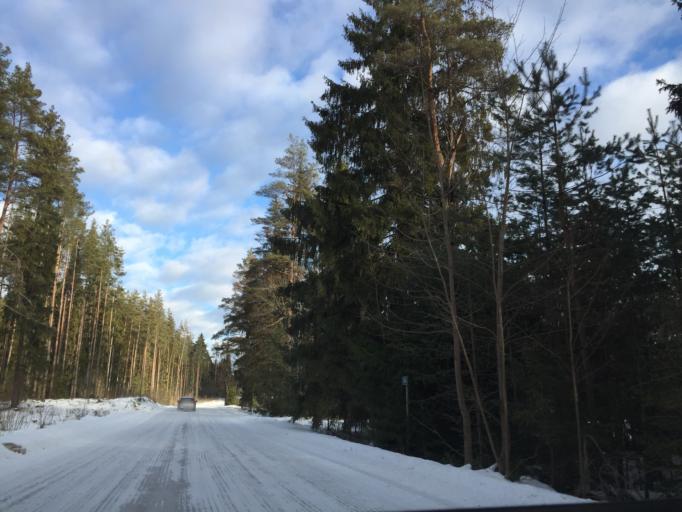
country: LV
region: Ogre
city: Jumprava
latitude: 56.5666
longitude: 24.9263
